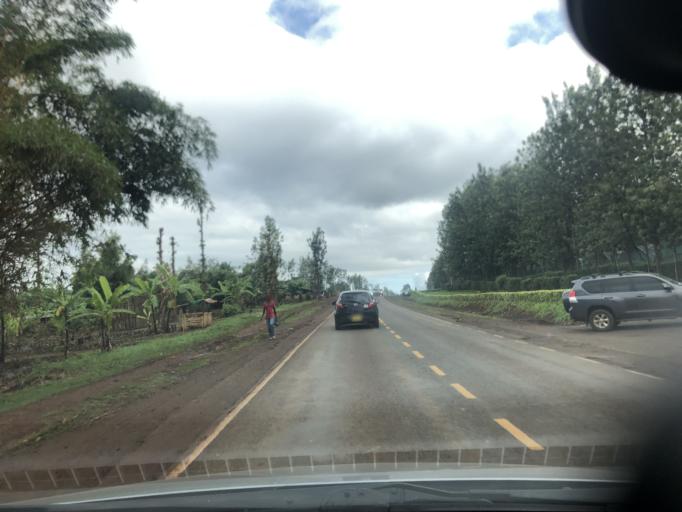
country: KE
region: Murang'a District
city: Maragua
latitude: -0.8292
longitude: 37.1376
